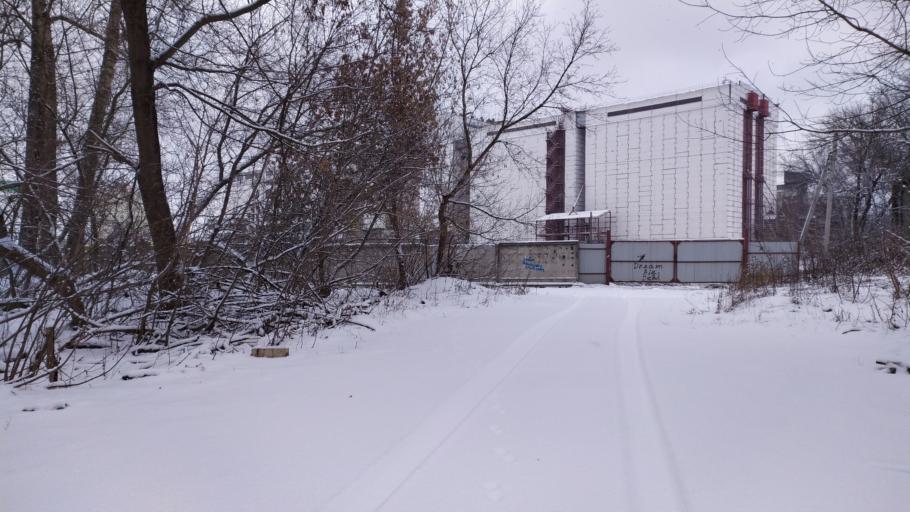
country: RU
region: Kursk
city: Kursk
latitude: 51.6563
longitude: 36.1466
